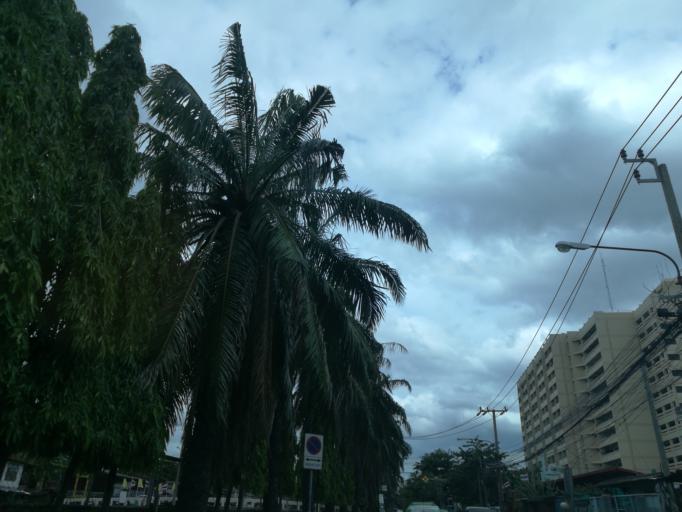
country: TH
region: Bangkok
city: Bang Sue
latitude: 13.7985
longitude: 100.5350
